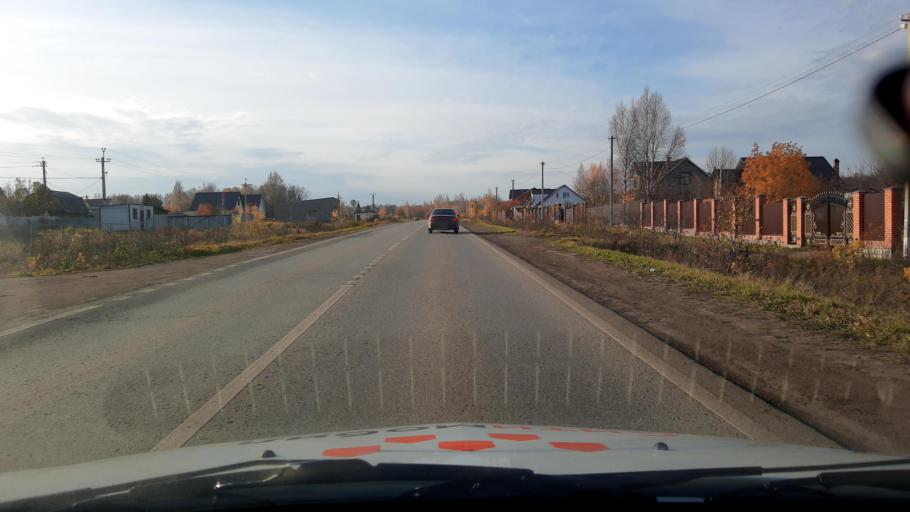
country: RU
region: Bashkortostan
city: Kabakovo
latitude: 54.7127
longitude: 56.1697
